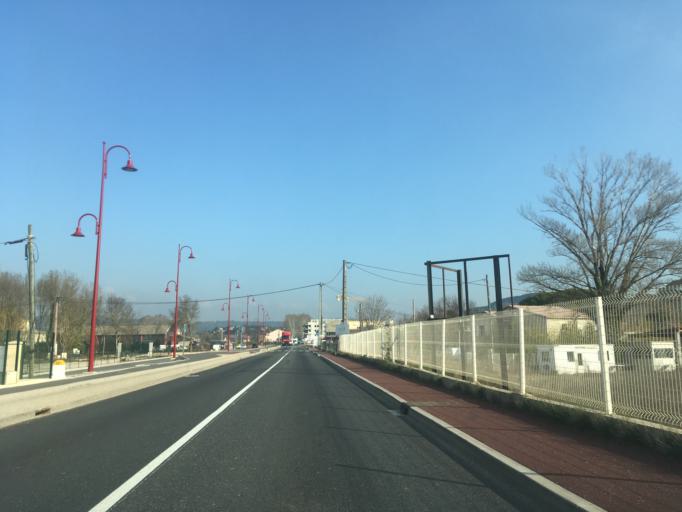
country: FR
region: Provence-Alpes-Cote d'Azur
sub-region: Departement du Var
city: Vidauban
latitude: 43.4205
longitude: 6.4248
